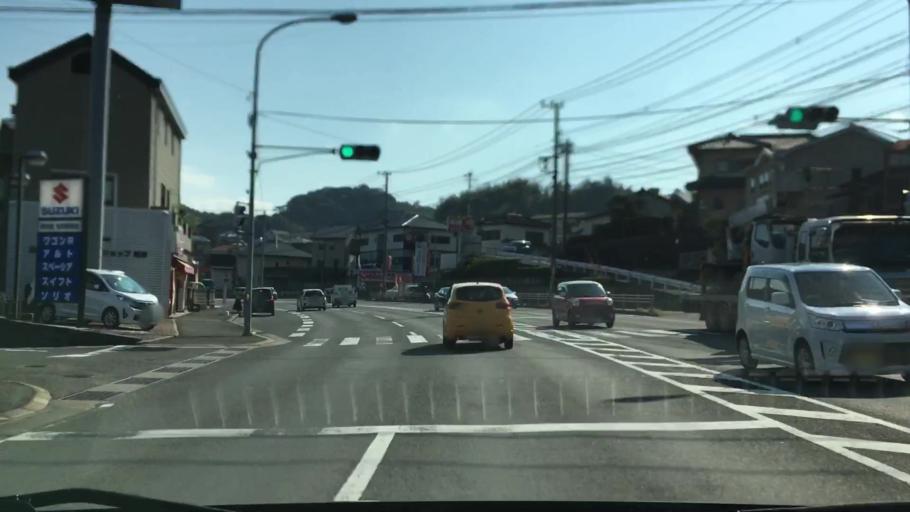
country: JP
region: Nagasaki
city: Togitsu
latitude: 32.8372
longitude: 129.8377
